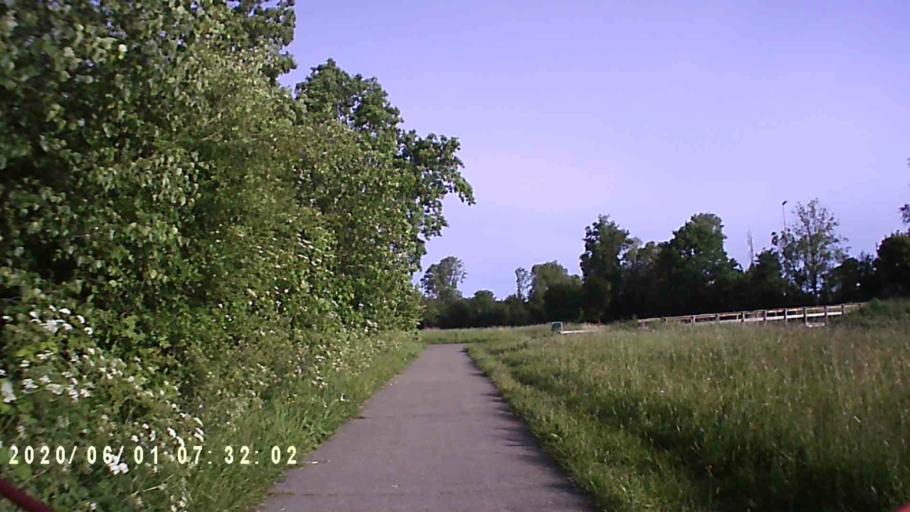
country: NL
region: Friesland
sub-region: Gemeente Dongeradeel
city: Dokkum
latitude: 53.3117
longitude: 5.9986
